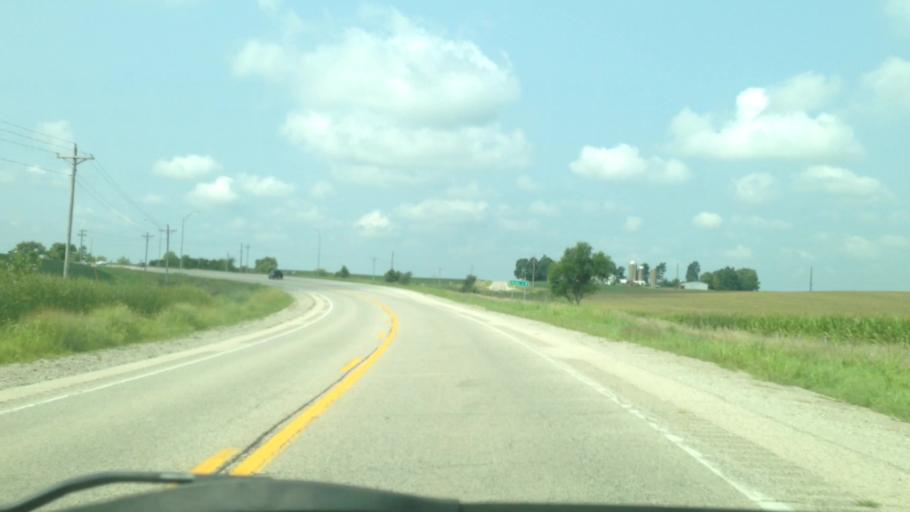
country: US
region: Iowa
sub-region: Benton County
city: Walford
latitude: 41.8762
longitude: -91.8645
